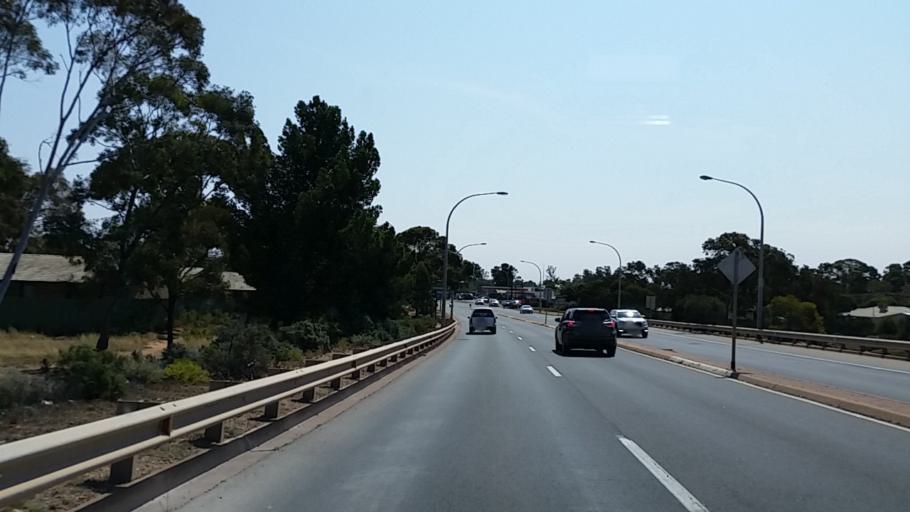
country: AU
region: South Australia
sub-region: Port Augusta
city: Port Augusta
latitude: -32.5020
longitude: 137.7803
